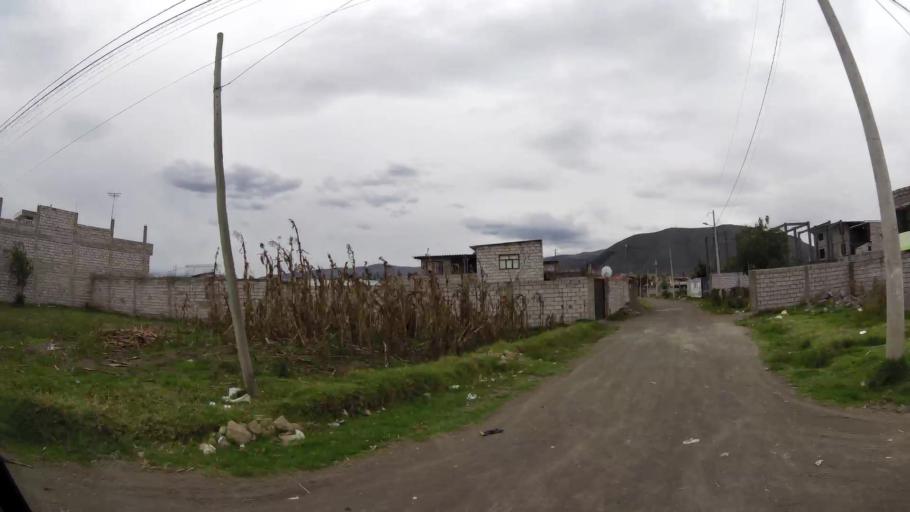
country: EC
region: Cotopaxi
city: Latacunga
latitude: -0.9600
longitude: -78.6079
